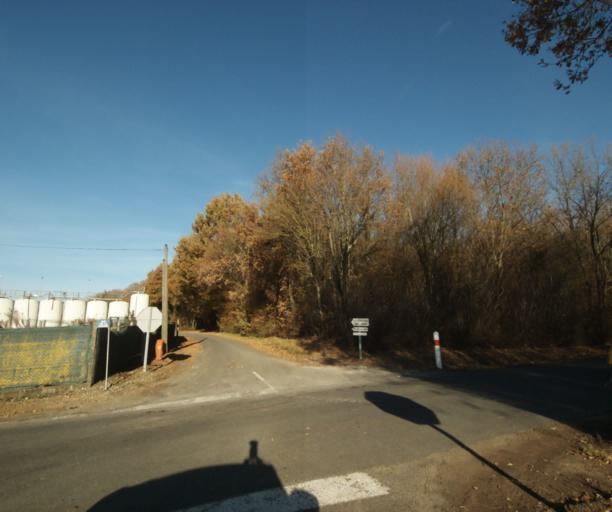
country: FR
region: Poitou-Charentes
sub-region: Departement de la Charente-Maritime
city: Cherac
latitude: 45.7128
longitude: -0.4719
